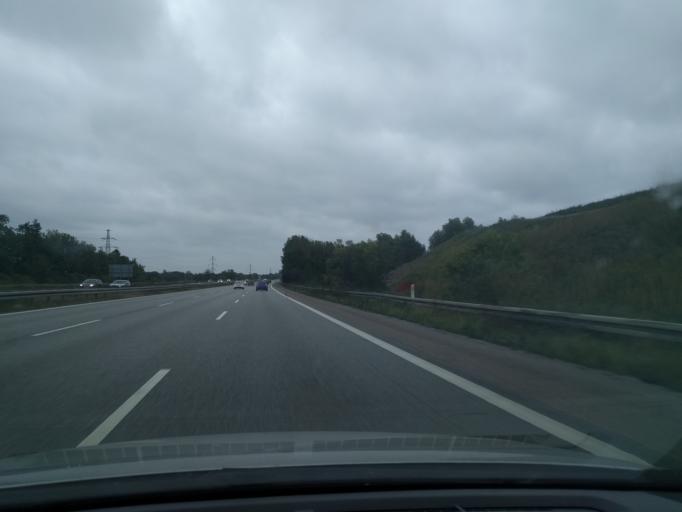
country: DK
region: Capital Region
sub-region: Vallensbaek Kommune
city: Vallensbaek
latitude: 55.6223
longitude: 12.3626
